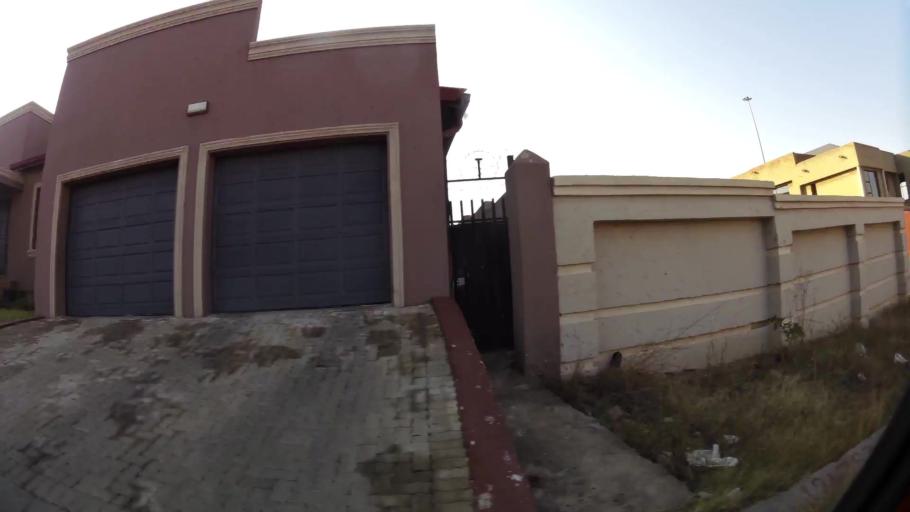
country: ZA
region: Gauteng
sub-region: City of Johannesburg Metropolitan Municipality
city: Johannesburg
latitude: -26.2564
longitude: 27.9610
